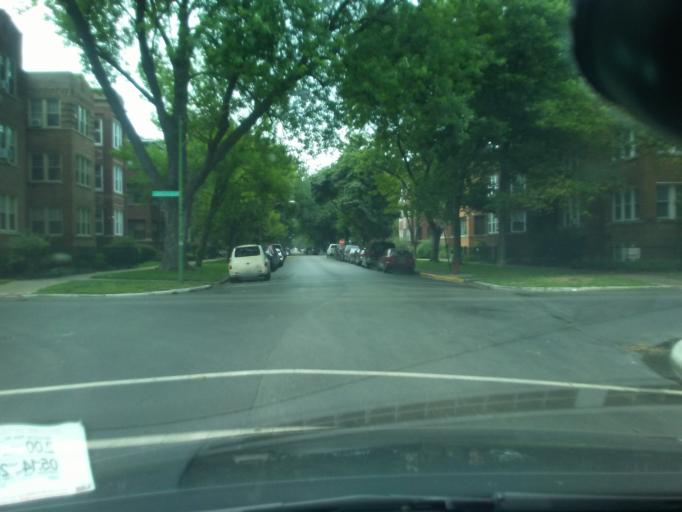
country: US
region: Illinois
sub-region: Cook County
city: Lincolnwood
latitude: 41.9723
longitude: -87.6777
